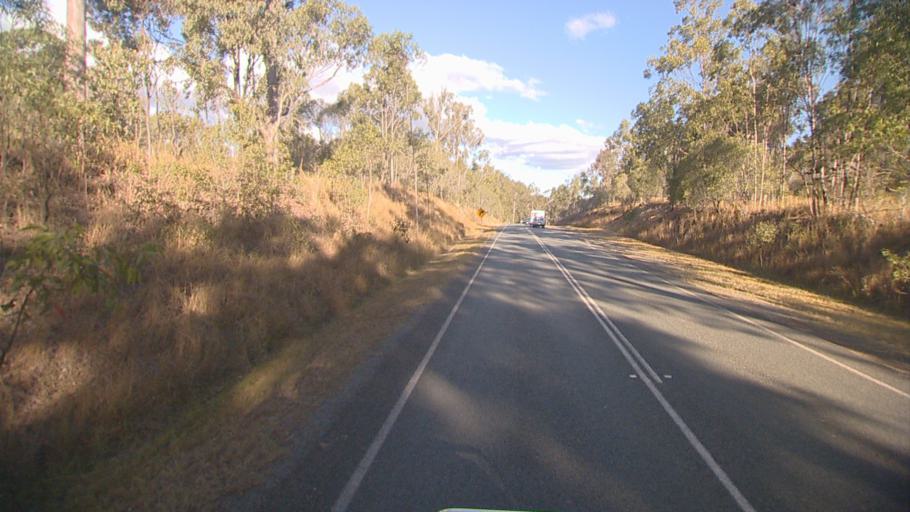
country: AU
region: Queensland
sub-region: Logan
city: Cedar Vale
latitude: -27.9000
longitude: 153.0899
